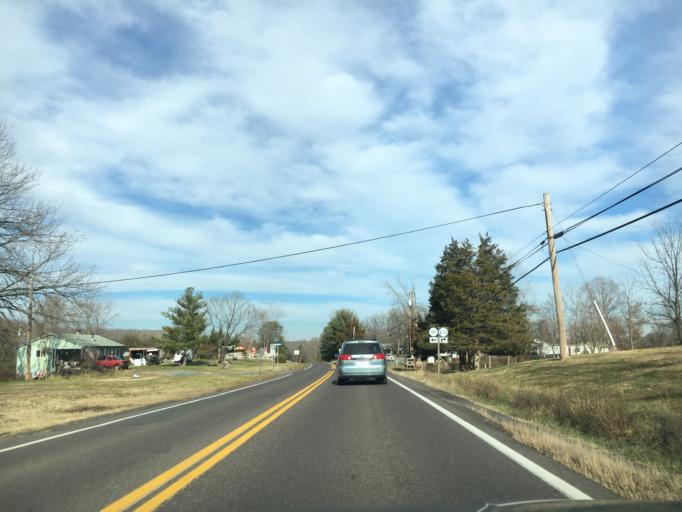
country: US
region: Virginia
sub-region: Culpeper County
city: Culpeper
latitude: 38.5303
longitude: -77.9805
